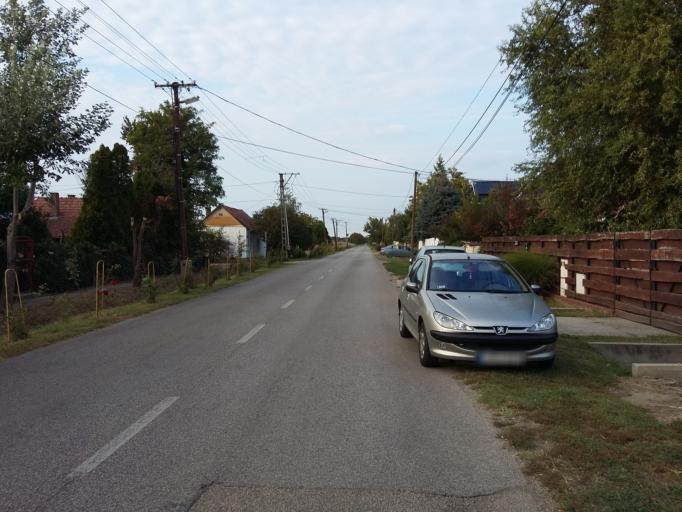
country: HU
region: Csongrad
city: Szeged
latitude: 46.2093
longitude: 20.1075
